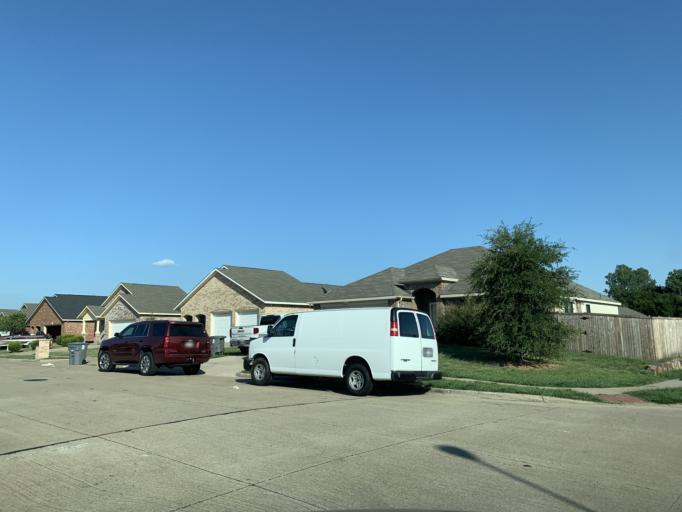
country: US
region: Texas
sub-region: Dallas County
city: Hutchins
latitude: 32.6575
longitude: -96.7643
